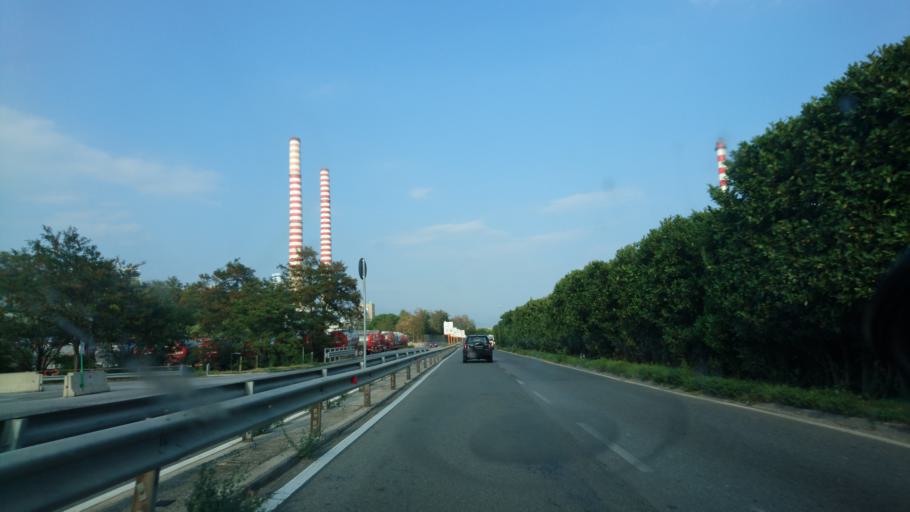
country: IT
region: Liguria
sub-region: Provincia di Savona
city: Vado Centro
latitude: 44.2703
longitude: 8.4278
